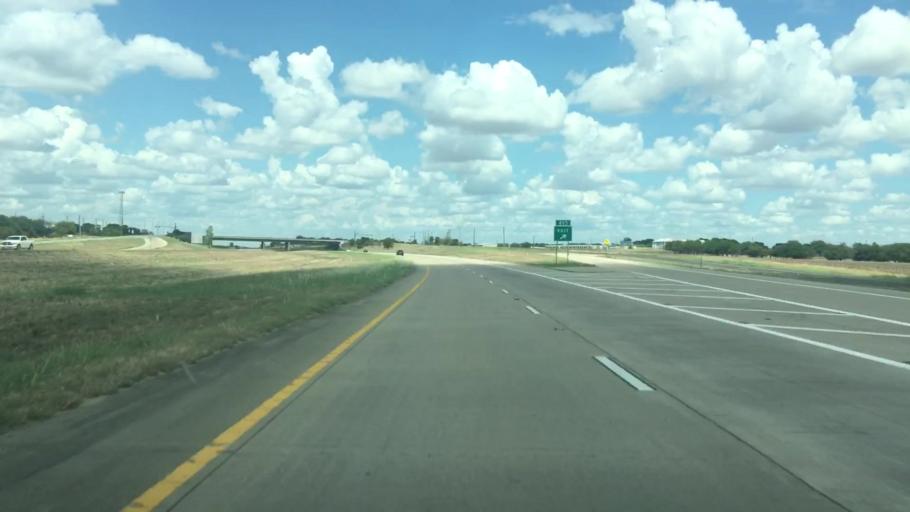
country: US
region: Texas
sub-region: Williamson County
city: Georgetown
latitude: 30.6363
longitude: -97.6282
